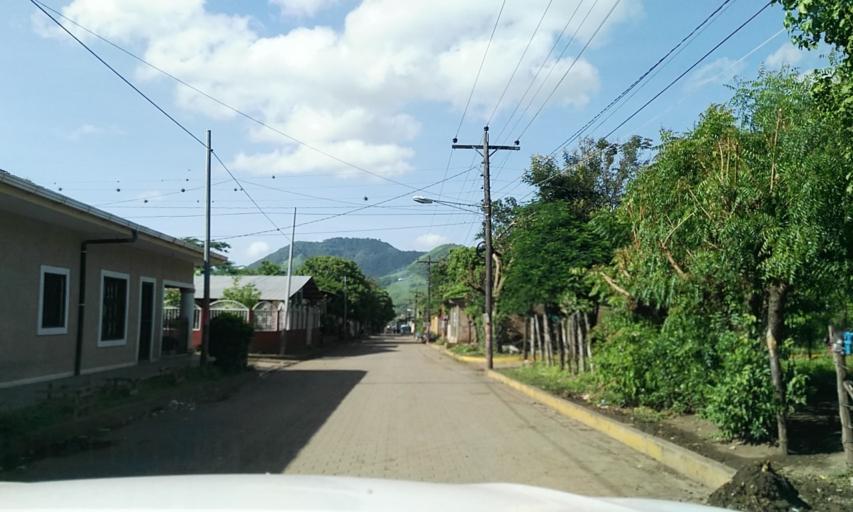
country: NI
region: Matagalpa
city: Terrabona
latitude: 12.7325
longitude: -85.9642
